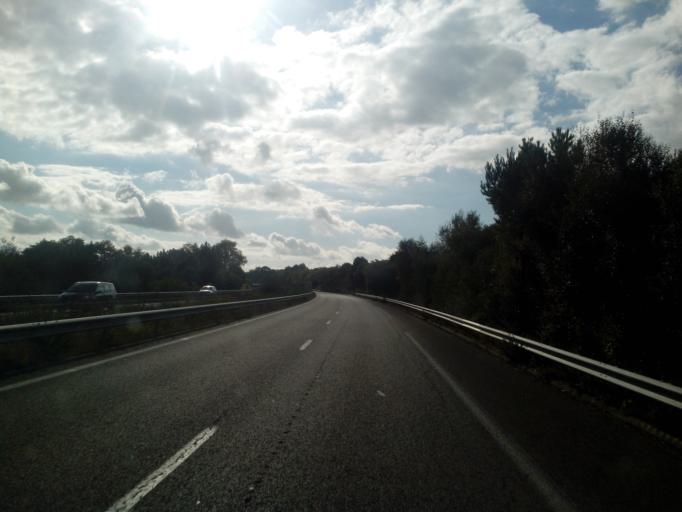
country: FR
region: Brittany
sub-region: Departement du Morbihan
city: Elven
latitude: 47.7604
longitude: -2.5370
